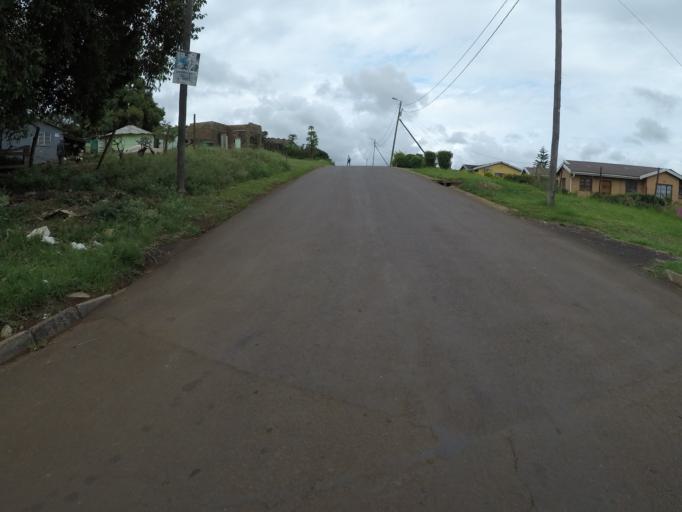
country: ZA
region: KwaZulu-Natal
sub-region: uThungulu District Municipality
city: Empangeni
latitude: -28.7713
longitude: 31.8684
